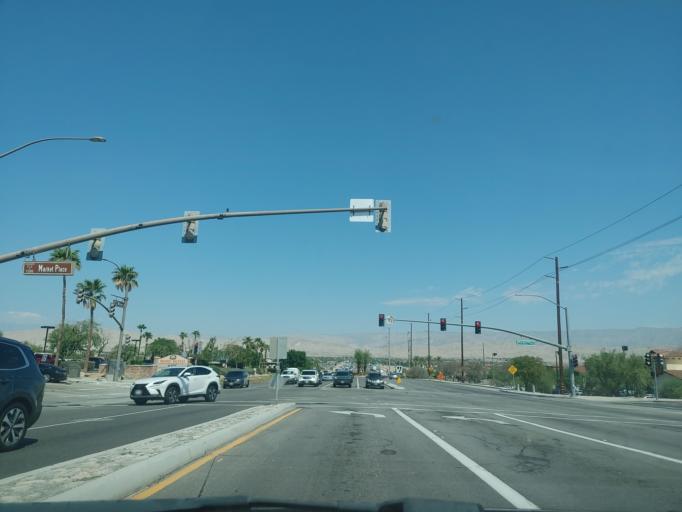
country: US
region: California
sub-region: Riverside County
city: Thousand Palms
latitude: 33.7989
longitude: -116.3882
